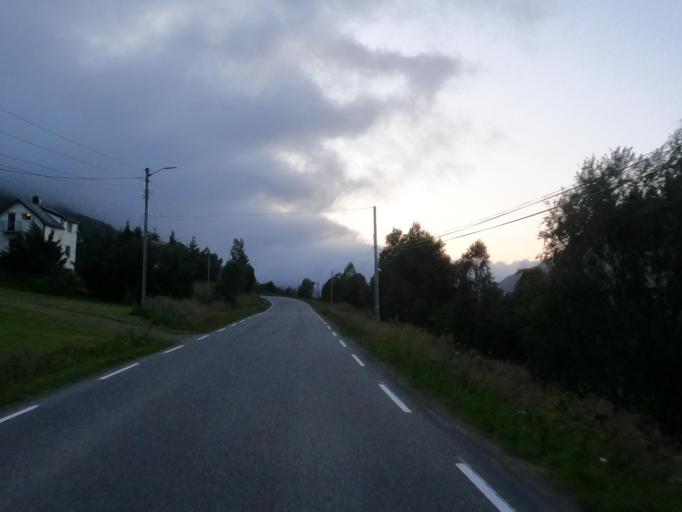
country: NO
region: Nordland
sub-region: Lodingen
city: Lodingen
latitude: 68.5744
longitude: 15.7951
